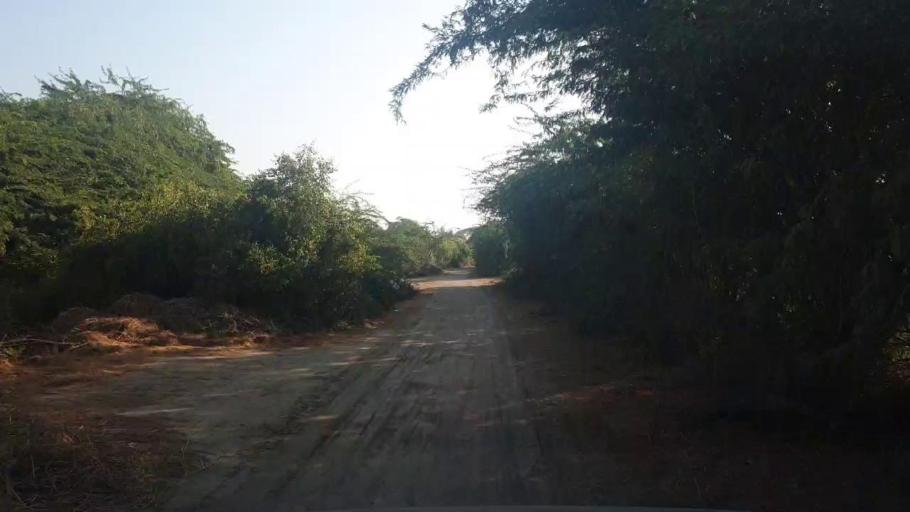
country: PK
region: Sindh
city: Tando Bago
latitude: 24.7450
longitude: 68.9286
